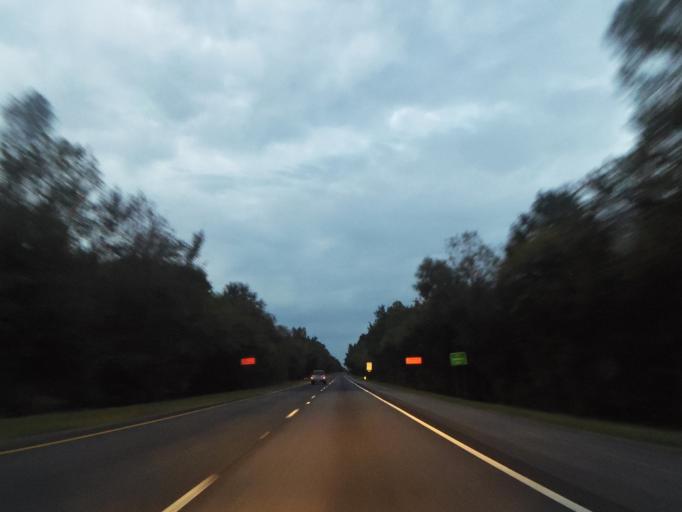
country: US
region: Alabama
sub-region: DeKalb County
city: Crossville
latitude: 34.1990
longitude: -85.9448
